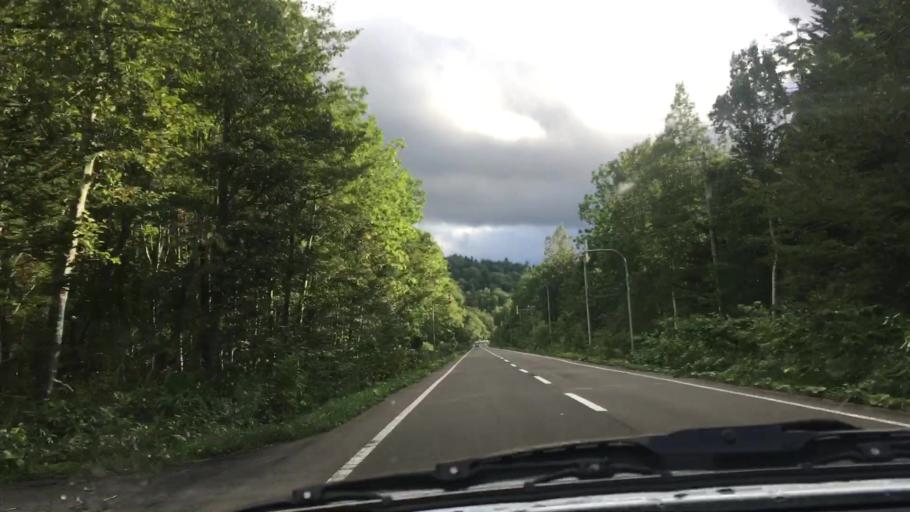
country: JP
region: Hokkaido
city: Shimo-furano
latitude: 43.0908
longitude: 142.6822
